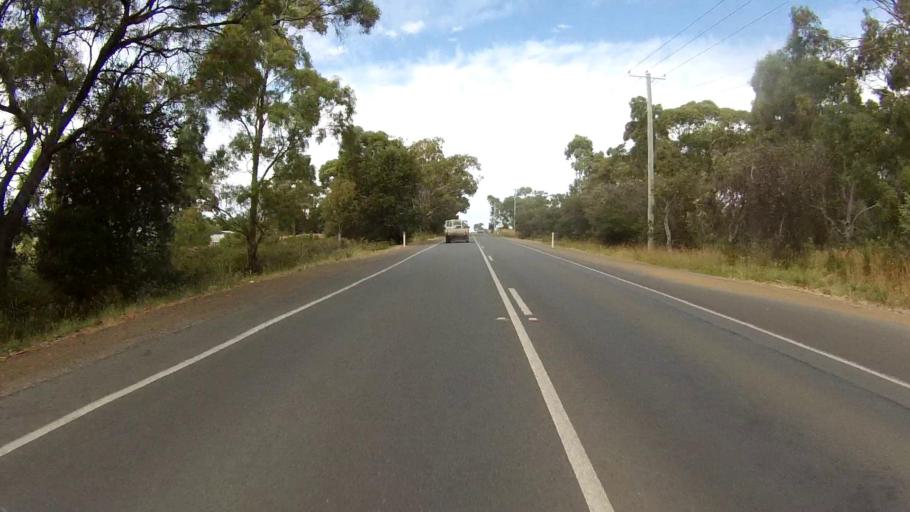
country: AU
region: Tasmania
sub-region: Clarence
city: Sandford
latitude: -42.9446
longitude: 147.4994
